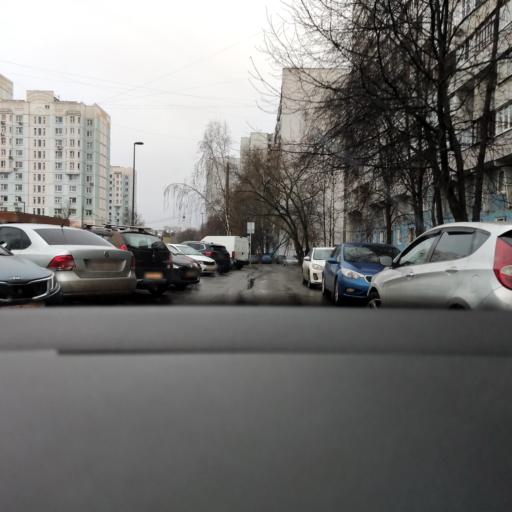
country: RU
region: Moscow
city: Kozeyevo
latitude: 55.8700
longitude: 37.6354
